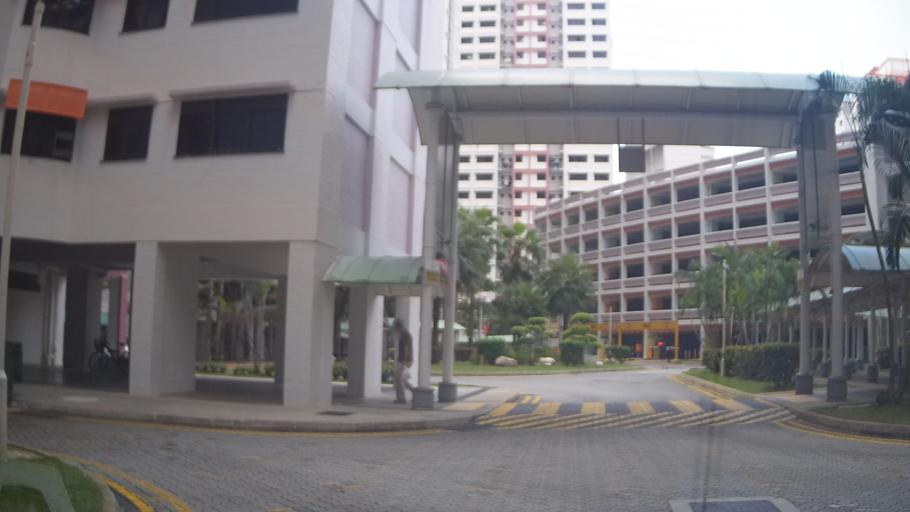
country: MY
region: Johor
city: Johor Bahru
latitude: 1.4029
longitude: 103.7518
